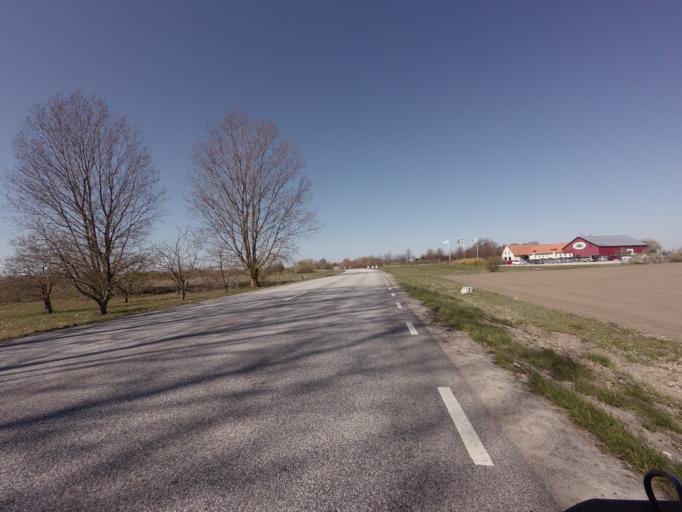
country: SE
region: Skane
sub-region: Vellinge Kommun
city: Vellinge
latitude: 55.4664
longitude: 13.0829
